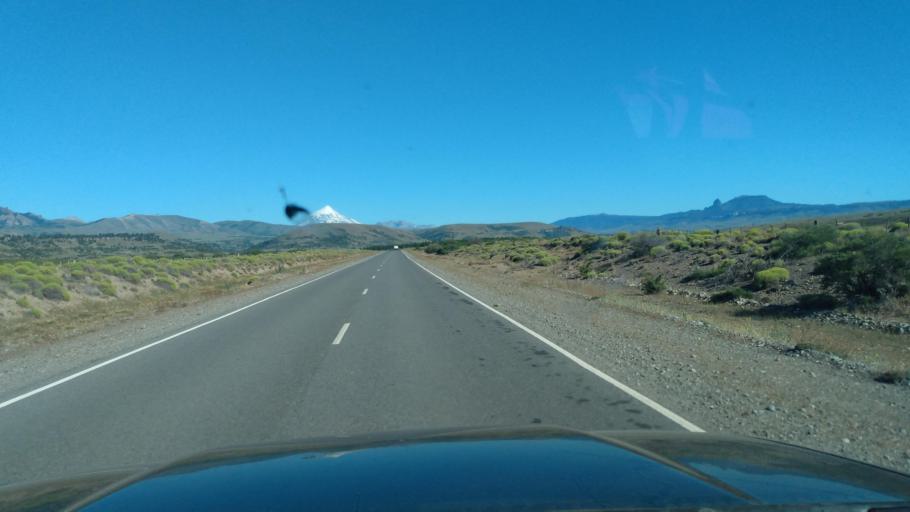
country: AR
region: Neuquen
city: Junin de los Andes
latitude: -39.8811
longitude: -71.1633
